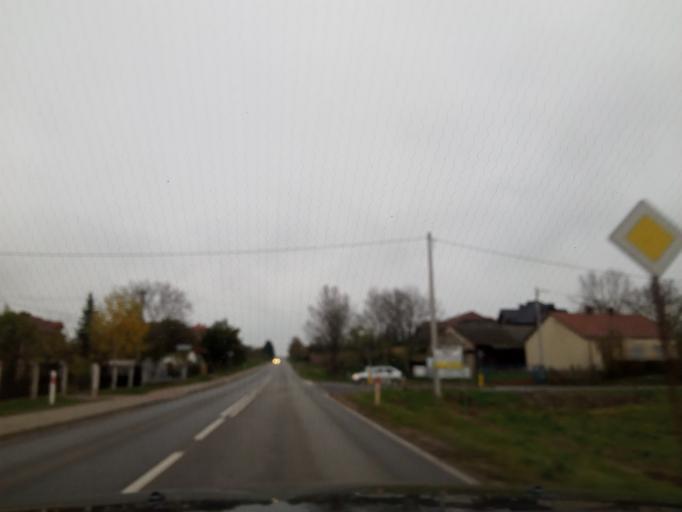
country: PL
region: Lesser Poland Voivodeship
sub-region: Powiat proszowicki
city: Proszowice
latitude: 50.2058
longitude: 20.3059
